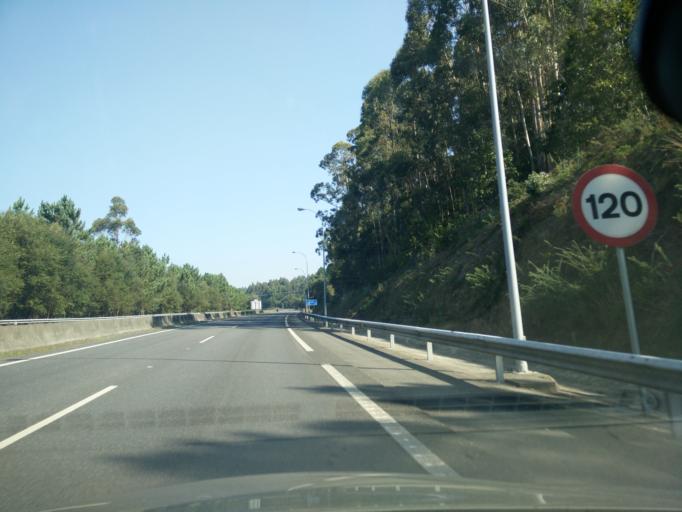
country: ES
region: Galicia
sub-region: Provincia da Coruna
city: Mino
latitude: 43.3786
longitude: -8.1821
